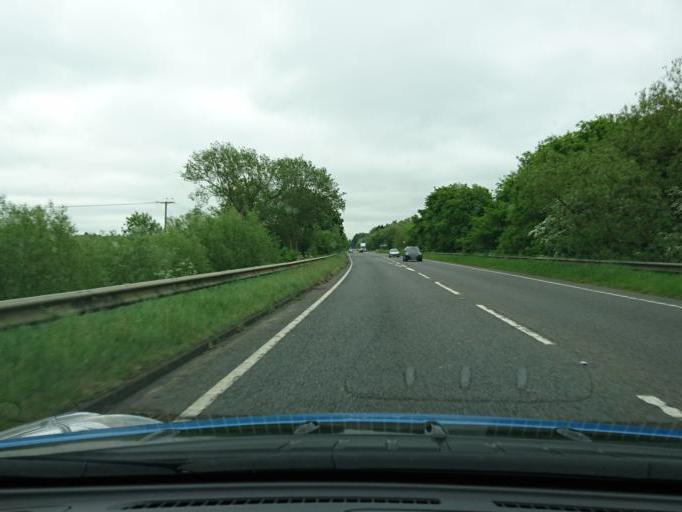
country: GB
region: England
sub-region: Oxfordshire
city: Frilford
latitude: 51.6858
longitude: -1.3839
